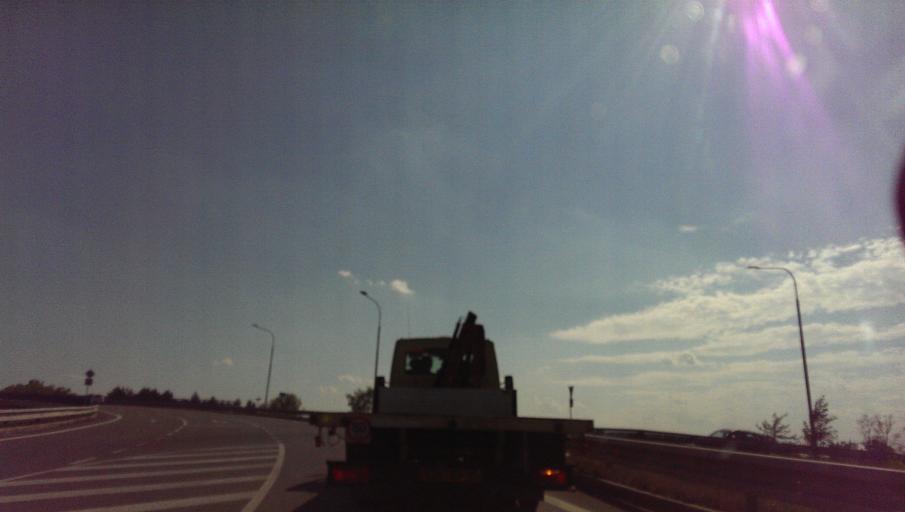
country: CZ
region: Zlin
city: Holesov
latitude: 49.3356
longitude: 17.5913
